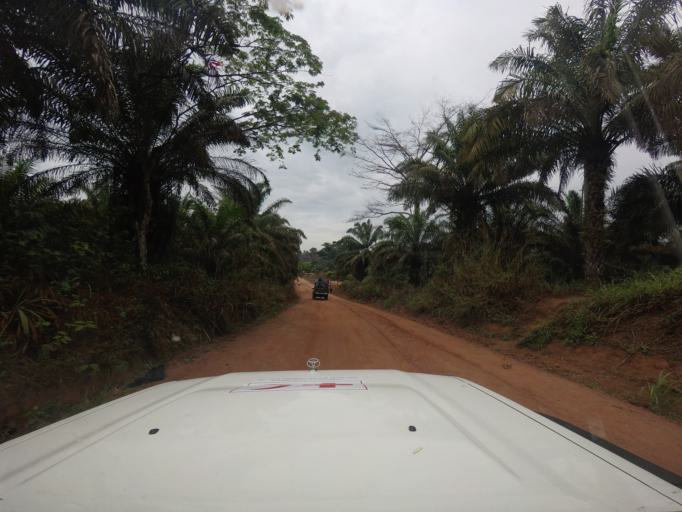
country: SL
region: Eastern Province
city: Buedu
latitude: 8.3118
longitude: -10.1400
